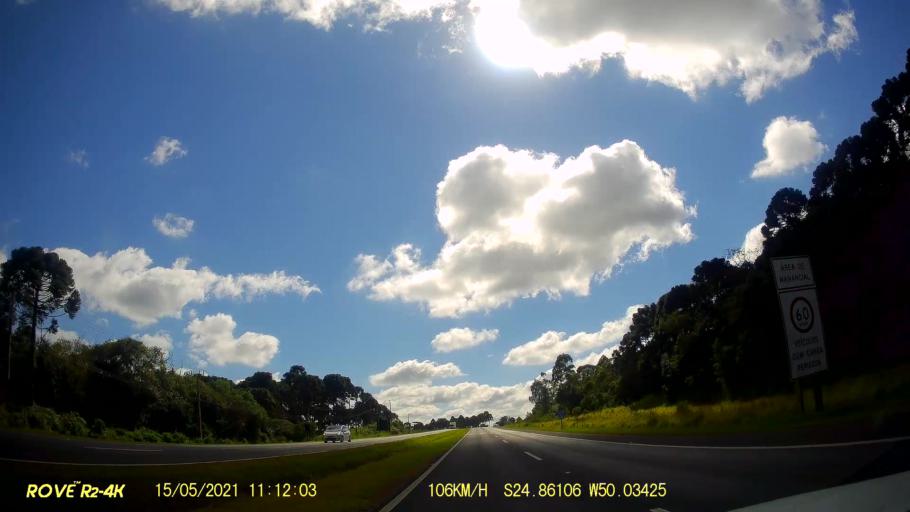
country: BR
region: Parana
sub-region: Castro
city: Castro
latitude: -24.8610
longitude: -50.0343
